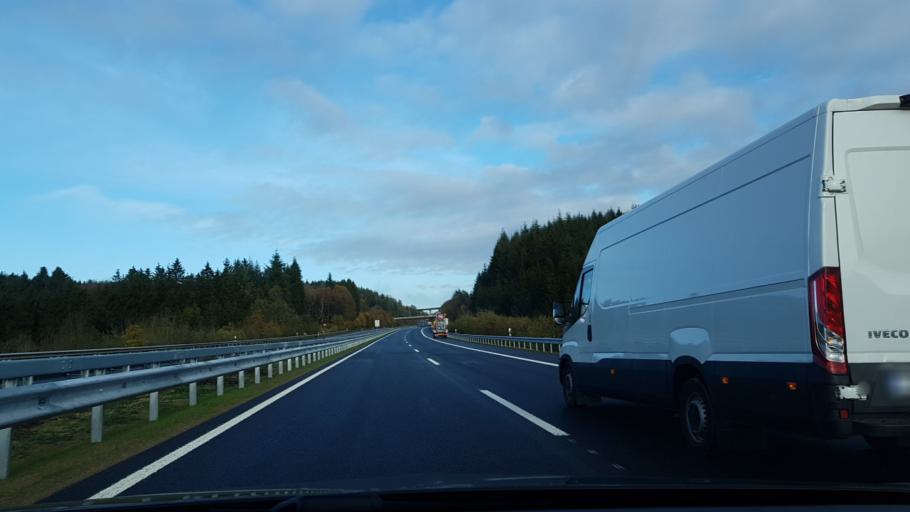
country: DE
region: Rheinland-Pfalz
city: Orlenbach
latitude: 50.1633
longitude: 6.3930
